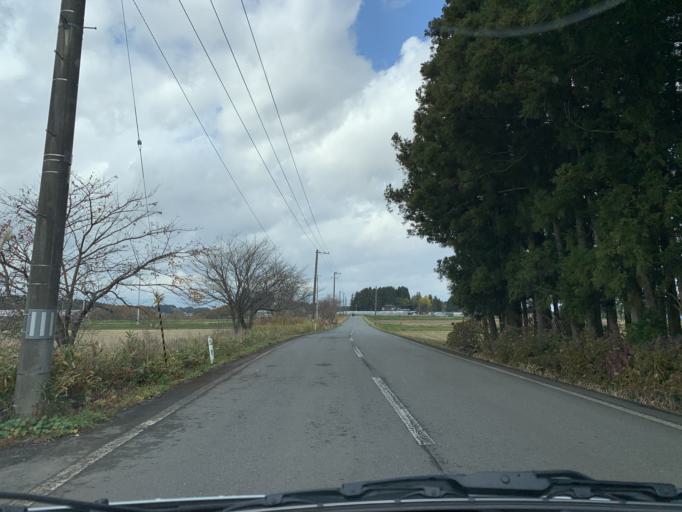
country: JP
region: Iwate
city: Mizusawa
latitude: 39.0670
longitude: 141.0789
